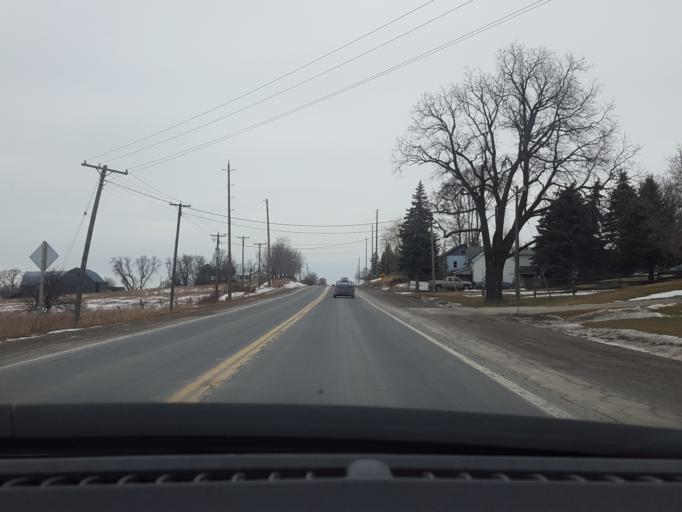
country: CA
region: Ontario
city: Newmarket
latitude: 44.1473
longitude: -79.4266
